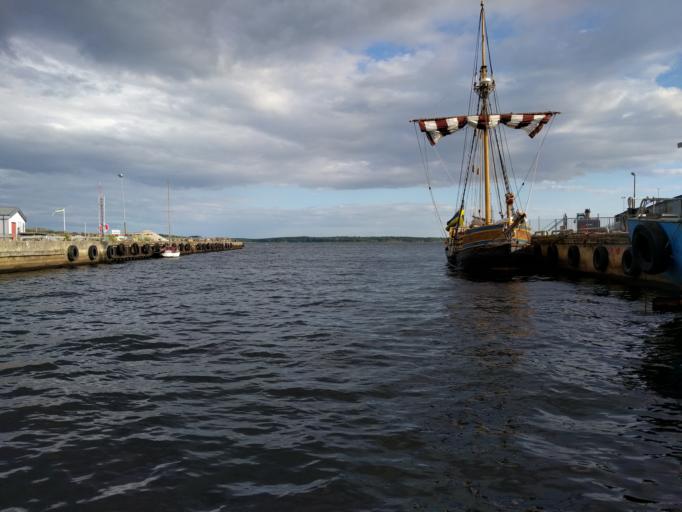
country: SE
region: Blekinge
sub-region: Ronneby Kommun
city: Ronneby
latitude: 56.1758
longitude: 15.3010
